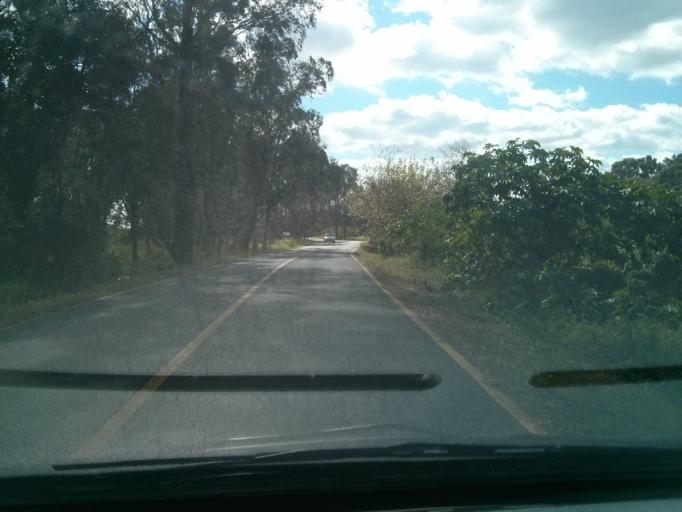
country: BR
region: Parana
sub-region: Sao Jose Dos Pinhais
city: Sao Jose dos Pinhais
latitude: -25.5383
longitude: -49.2262
